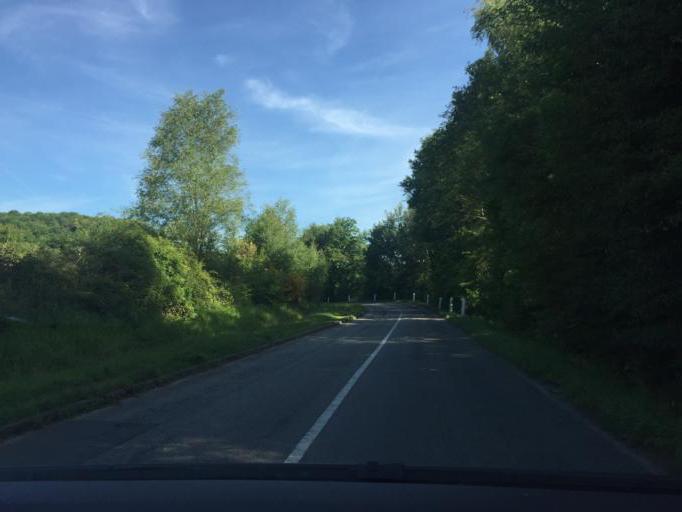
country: FR
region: Ile-de-France
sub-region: Departement de l'Essonne
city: Villiers-le-Bacle
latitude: 48.7116
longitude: 2.1200
